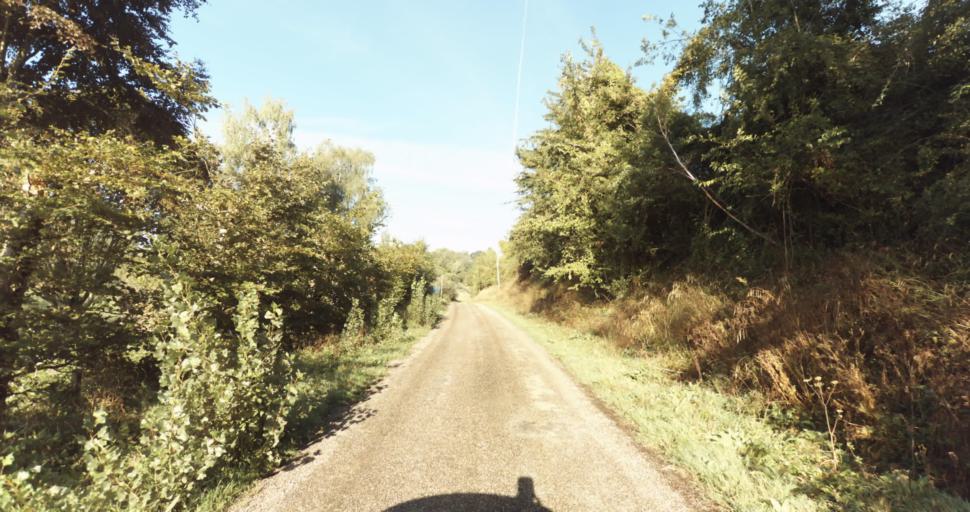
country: FR
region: Lower Normandy
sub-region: Departement de l'Orne
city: Vimoutiers
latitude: 48.9163
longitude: 0.1893
